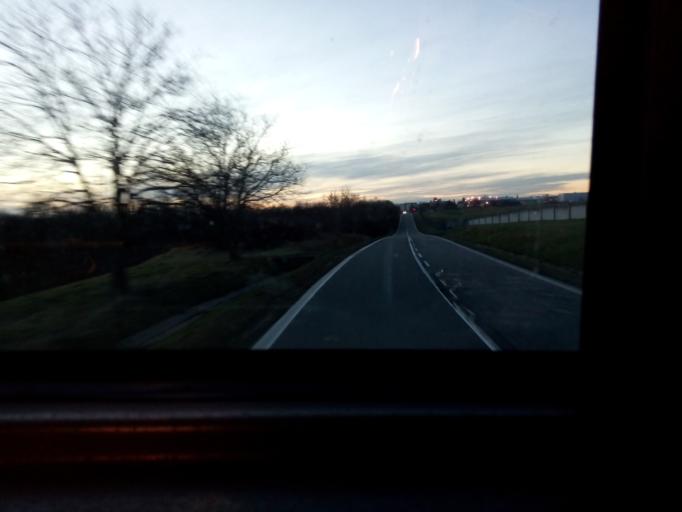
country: CZ
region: Central Bohemia
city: Tuchomerice
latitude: 50.1087
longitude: 14.2856
